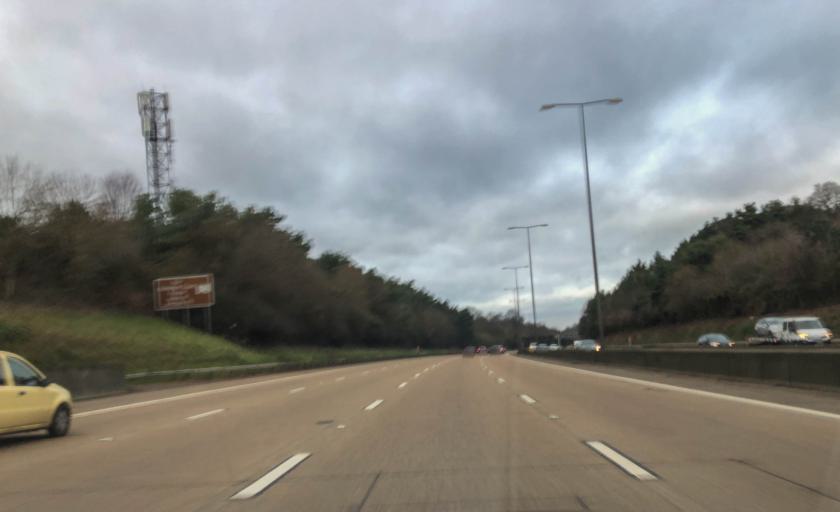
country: GB
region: England
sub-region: Surrey
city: Headley
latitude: 51.2721
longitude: -0.2565
